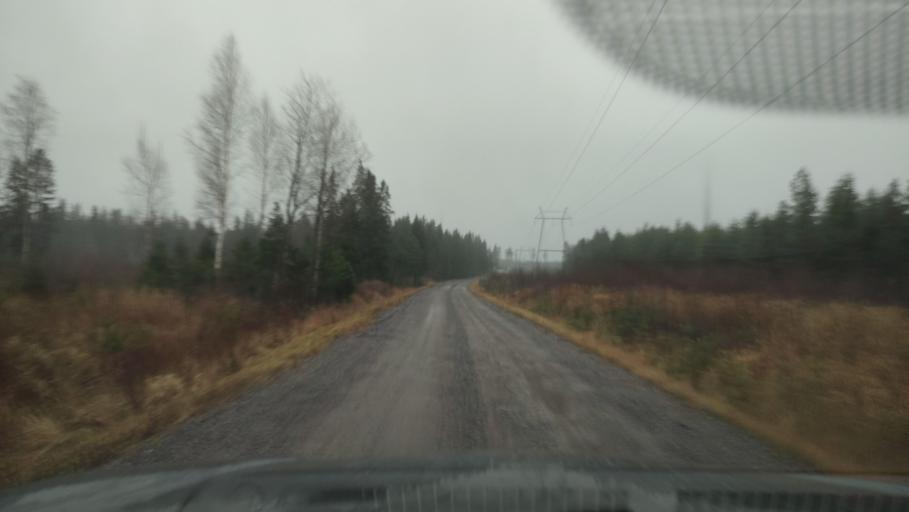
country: FI
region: Southern Ostrobothnia
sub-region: Suupohja
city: Karijoki
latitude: 62.2128
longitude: 21.7301
